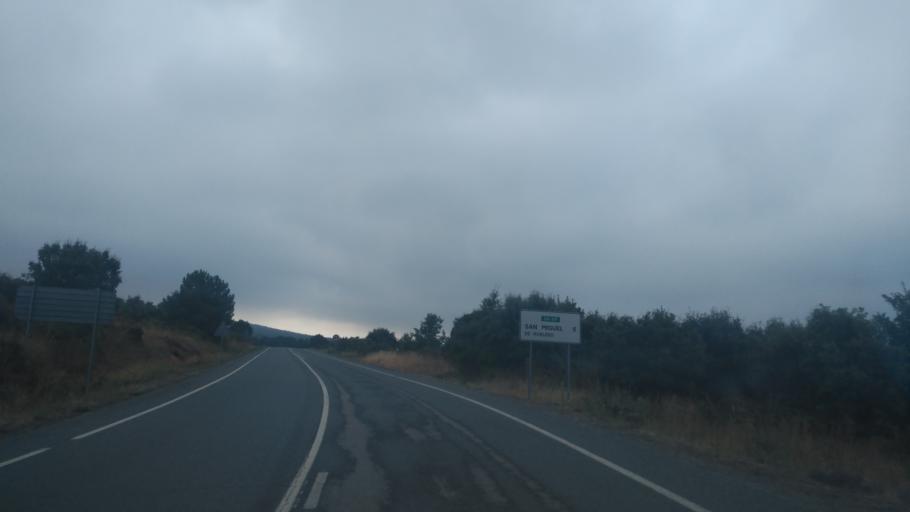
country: ES
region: Castille and Leon
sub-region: Provincia de Salamanca
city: Cereceda de la Sierra
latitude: 40.5726
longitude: -6.0784
